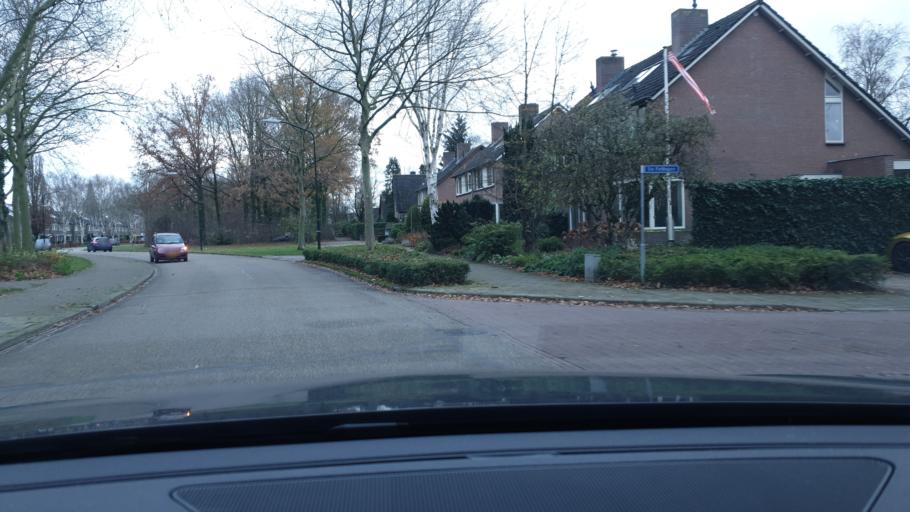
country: NL
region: North Brabant
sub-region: Gemeente Waalre
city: Waalre
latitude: 51.3905
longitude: 5.4391
